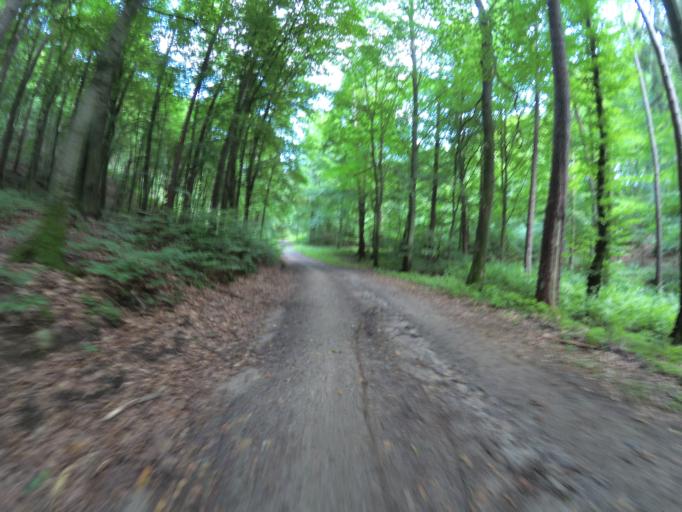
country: PL
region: Pomeranian Voivodeship
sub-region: Gdynia
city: Wielki Kack
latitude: 54.4894
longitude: 18.4561
